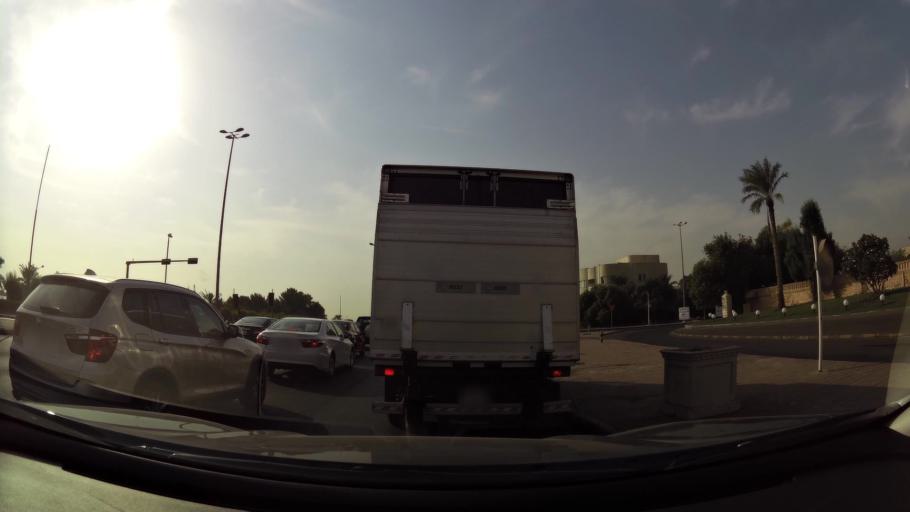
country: KW
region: Muhafazat Hawalli
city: Salwa
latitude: 29.2806
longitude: 48.0876
